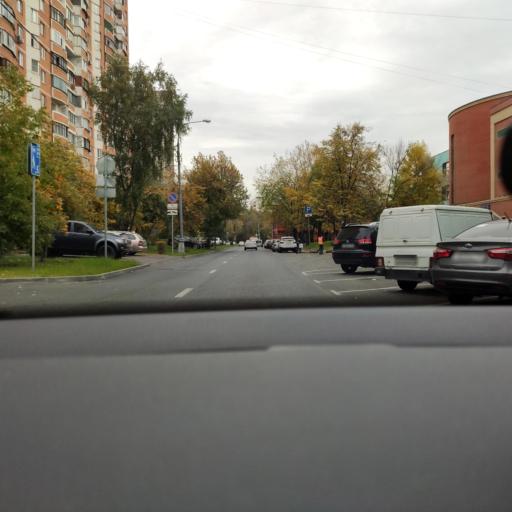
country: RU
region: Moscow
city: Kozeyevo
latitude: 55.8901
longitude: 37.6462
